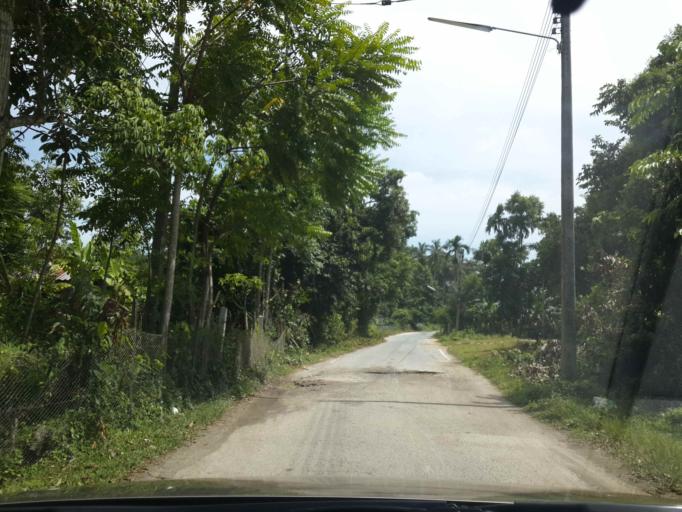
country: TH
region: Narathiwat
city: Rueso
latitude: 6.4024
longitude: 101.5164
